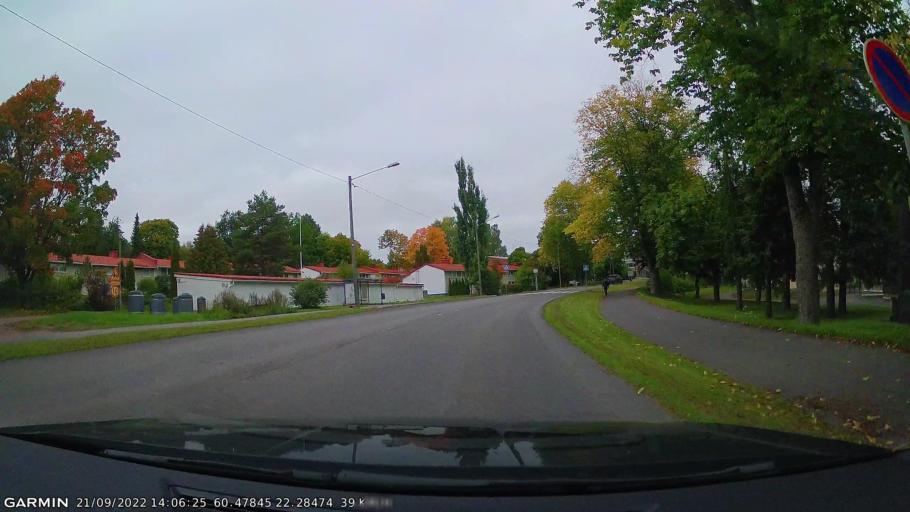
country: FI
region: Varsinais-Suomi
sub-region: Turku
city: Turku
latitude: 60.4784
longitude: 22.2847
